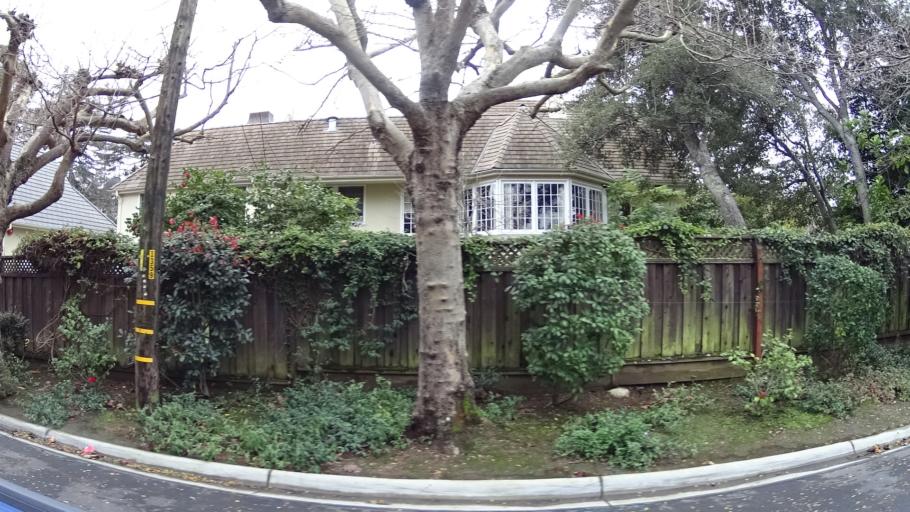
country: US
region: California
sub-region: San Mateo County
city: Burlingame
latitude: 37.5705
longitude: -122.3523
